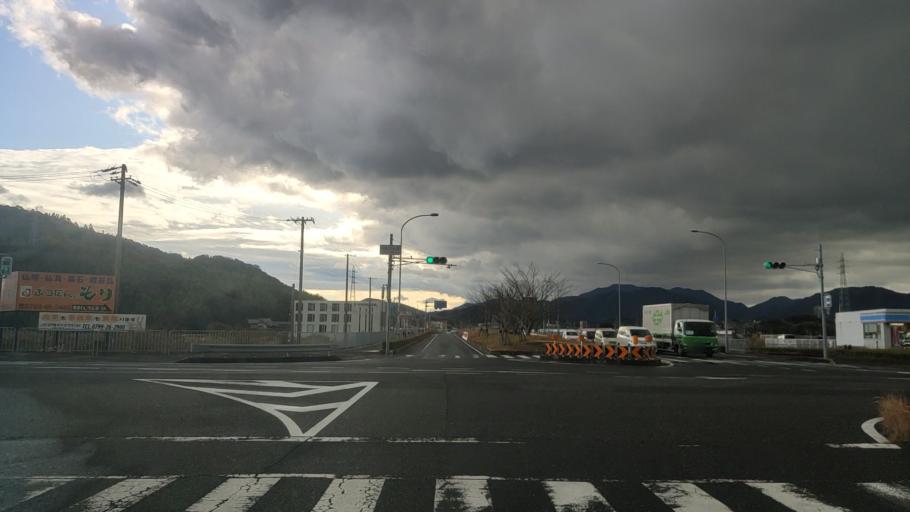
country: JP
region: Hyogo
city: Sumoto
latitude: 34.3386
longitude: 134.8471
